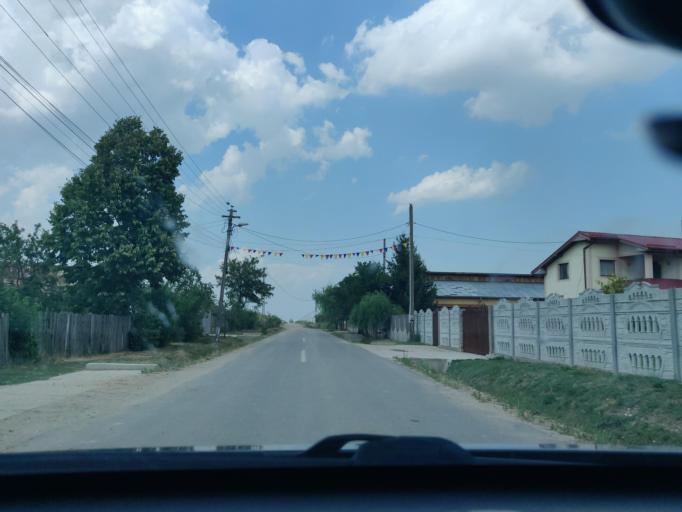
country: RO
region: Teleorman
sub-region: Comuna Sarbeni
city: Sarbeni
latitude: 44.4794
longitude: 25.3873
